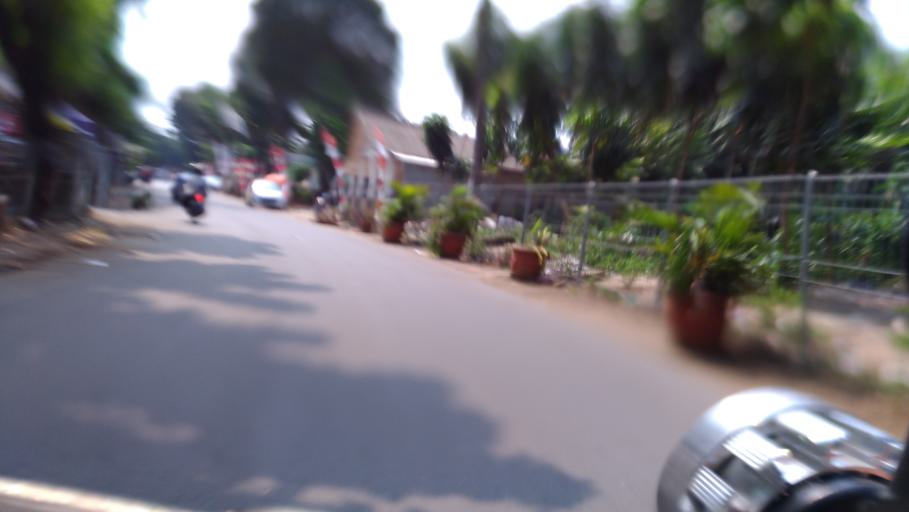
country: ID
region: West Java
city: Cileungsir
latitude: -6.3516
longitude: 106.8932
